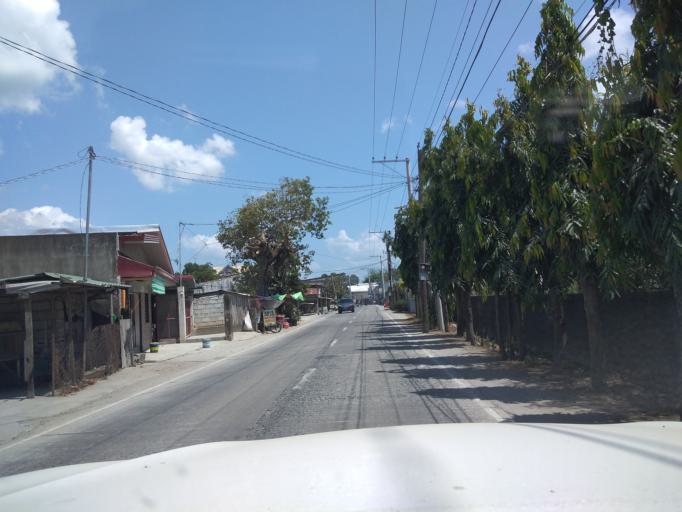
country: PH
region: Central Luzon
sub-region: Province of Pampanga
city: Bahay Pare
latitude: 15.0165
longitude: 120.8736
